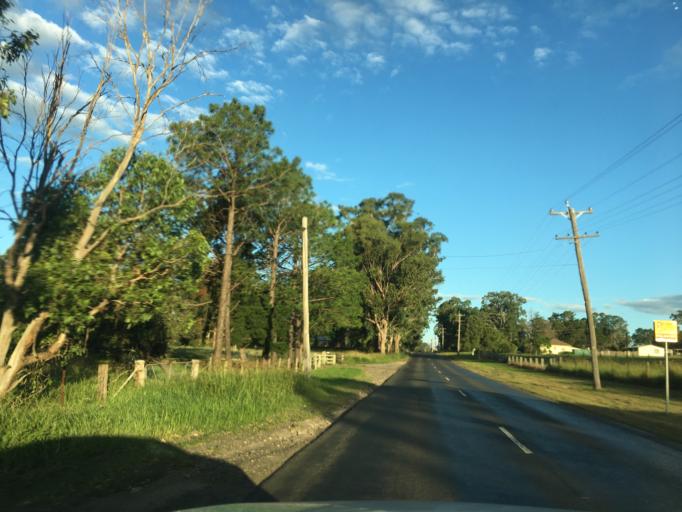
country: AU
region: New South Wales
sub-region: Campbelltown Municipality
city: Denham Court
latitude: -33.9638
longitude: 150.8074
